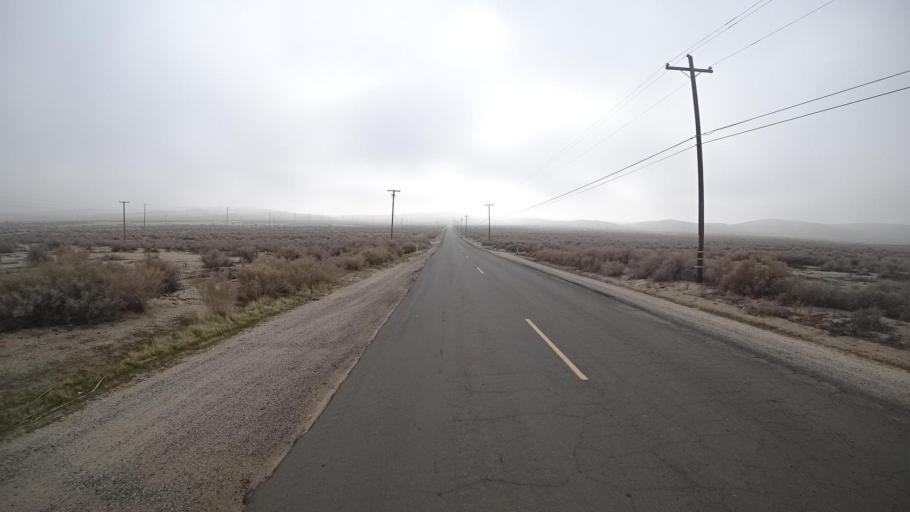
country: US
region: California
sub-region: Kern County
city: Ford City
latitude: 35.1868
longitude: -119.4290
